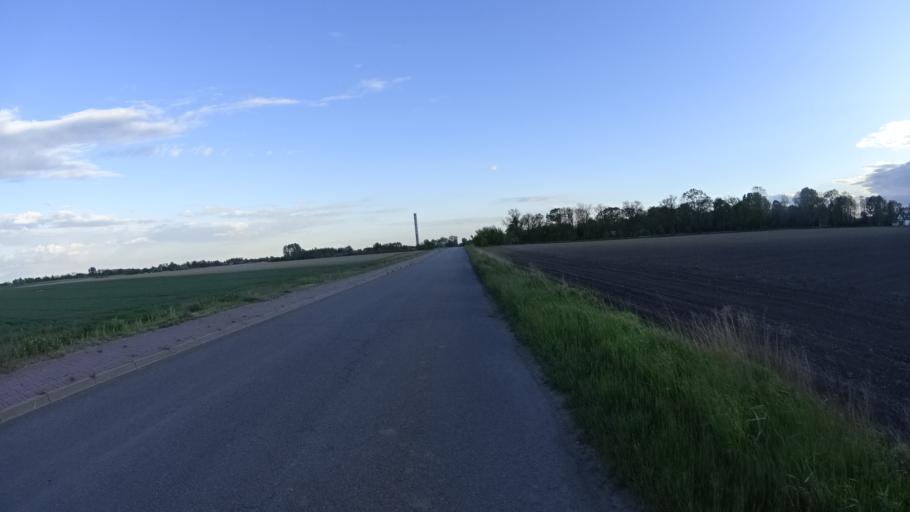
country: PL
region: Masovian Voivodeship
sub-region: Powiat warszawski zachodni
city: Jozefow
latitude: 52.2019
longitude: 20.7442
